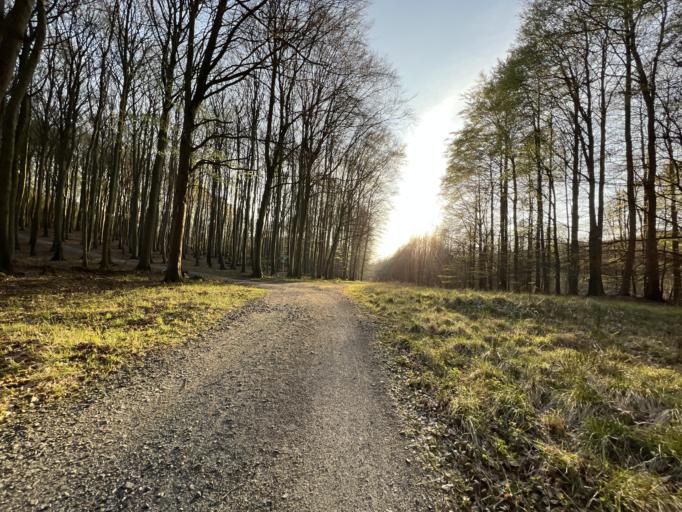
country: DE
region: Mecklenburg-Vorpommern
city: Sassnitz
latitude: 54.5361
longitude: 13.6592
